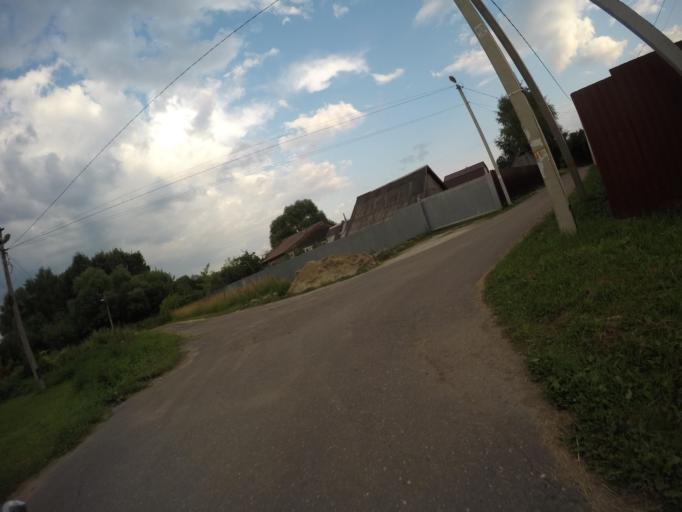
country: RU
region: Moskovskaya
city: Rechitsy
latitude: 55.5952
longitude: 38.5083
